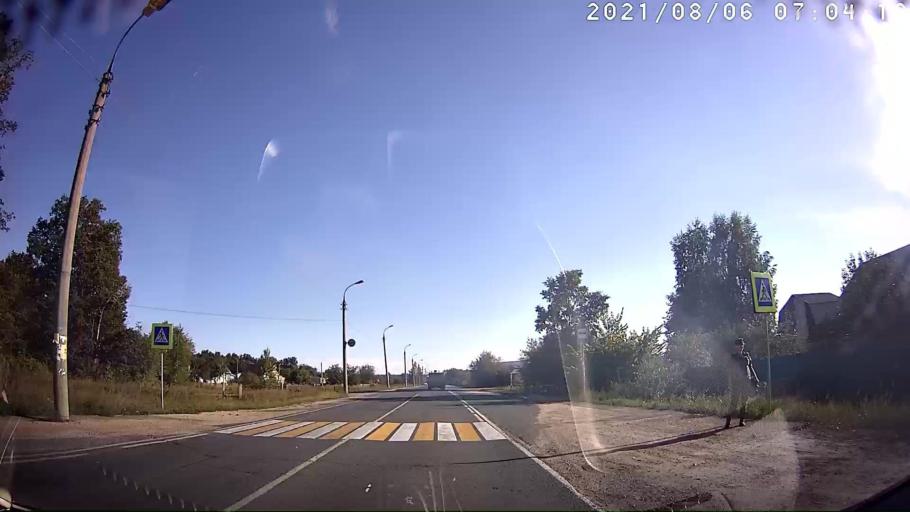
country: RU
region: Mariy-El
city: Yoshkar-Ola
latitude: 56.5459
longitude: 47.9816
